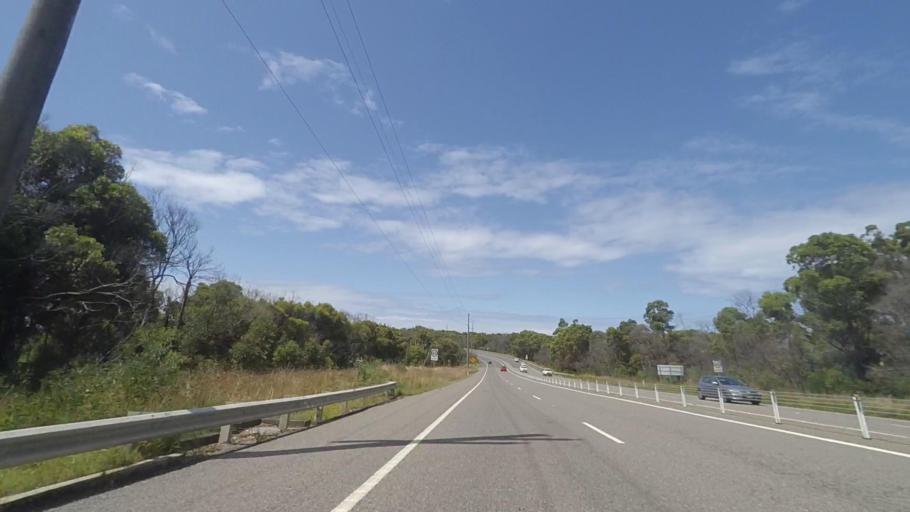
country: AU
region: New South Wales
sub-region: Wyong Shire
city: Kingfisher Shores
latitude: -33.1648
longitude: 151.6105
